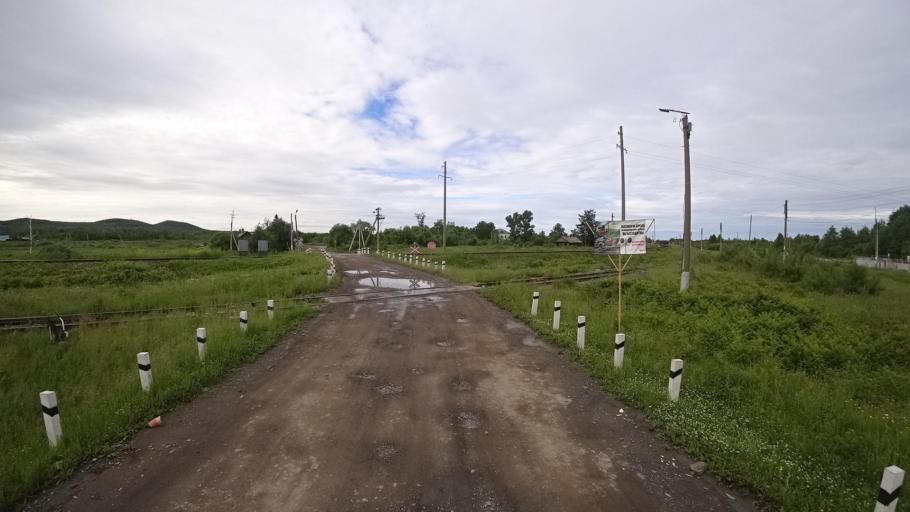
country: RU
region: Khabarovsk Krai
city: Amursk
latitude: 49.9044
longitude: 136.1436
